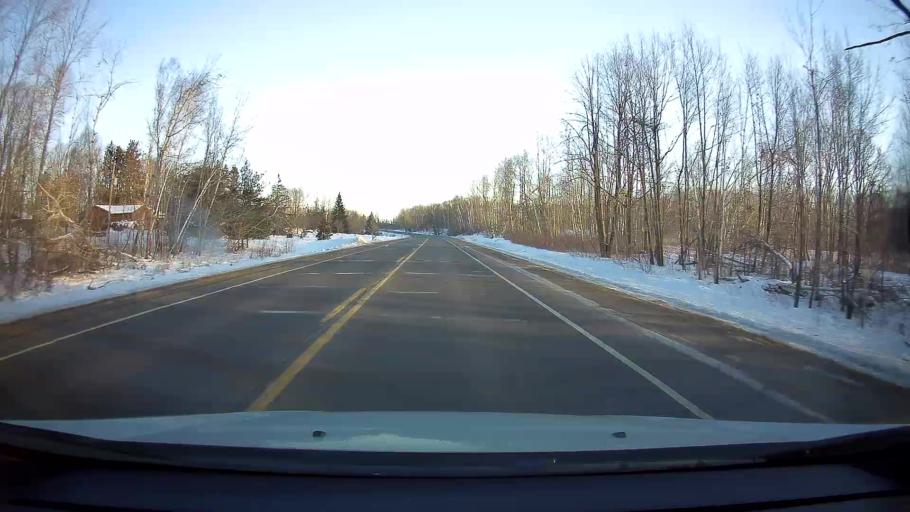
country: US
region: Wisconsin
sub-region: Barron County
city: Turtle Lake
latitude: 45.4179
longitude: -92.1314
